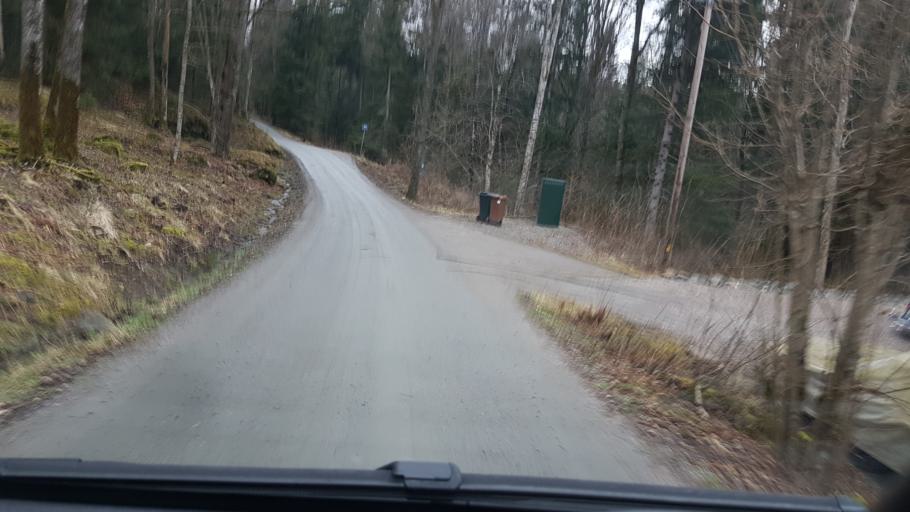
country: SE
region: Vaestra Goetaland
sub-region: Lerums Kommun
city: Stenkullen
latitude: 57.7970
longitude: 12.3912
